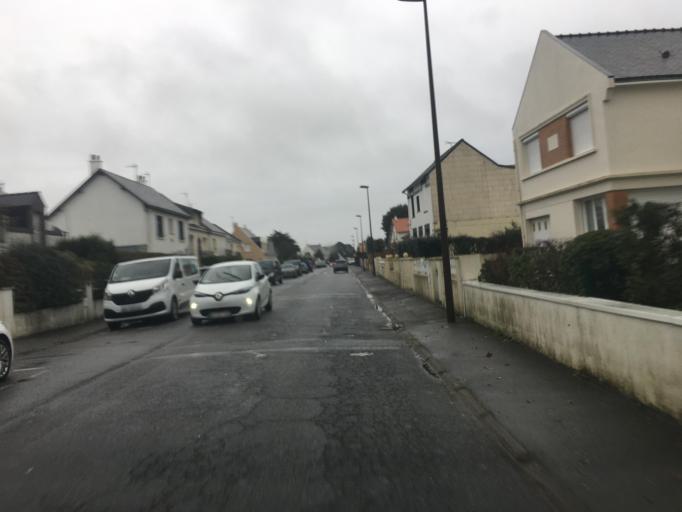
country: FR
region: Pays de la Loire
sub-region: Departement de la Loire-Atlantique
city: Guerande
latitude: 47.3310
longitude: -2.4237
